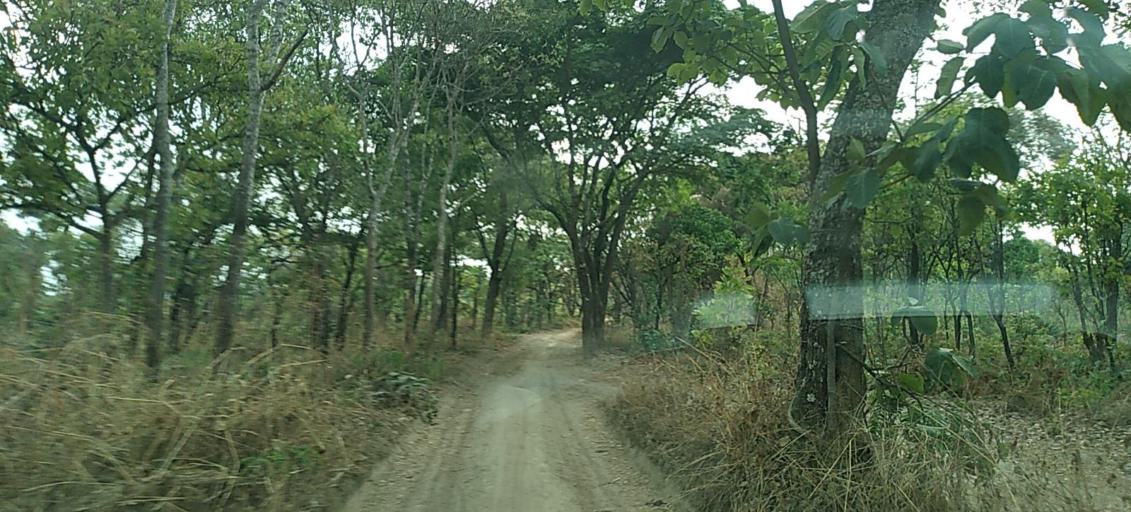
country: ZM
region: North-Western
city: Solwezi
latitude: -12.0976
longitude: 26.2787
